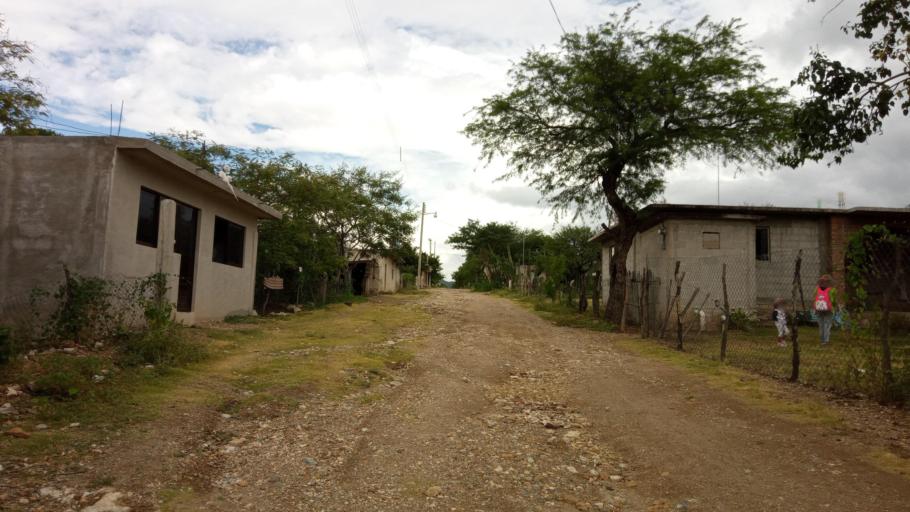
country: MX
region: Puebla
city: Totoltepec de Guerrero
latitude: 18.2959
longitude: -97.7756
